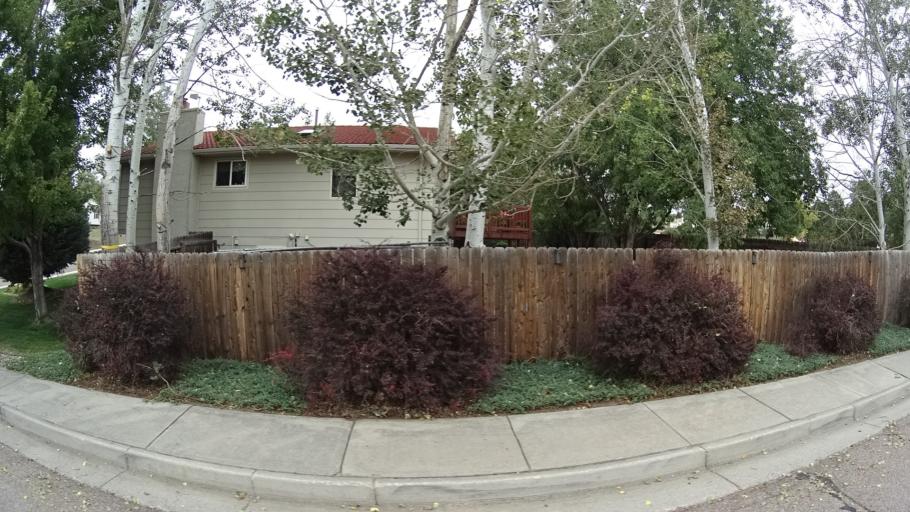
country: US
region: Colorado
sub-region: El Paso County
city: Cimarron Hills
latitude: 38.9026
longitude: -104.7296
